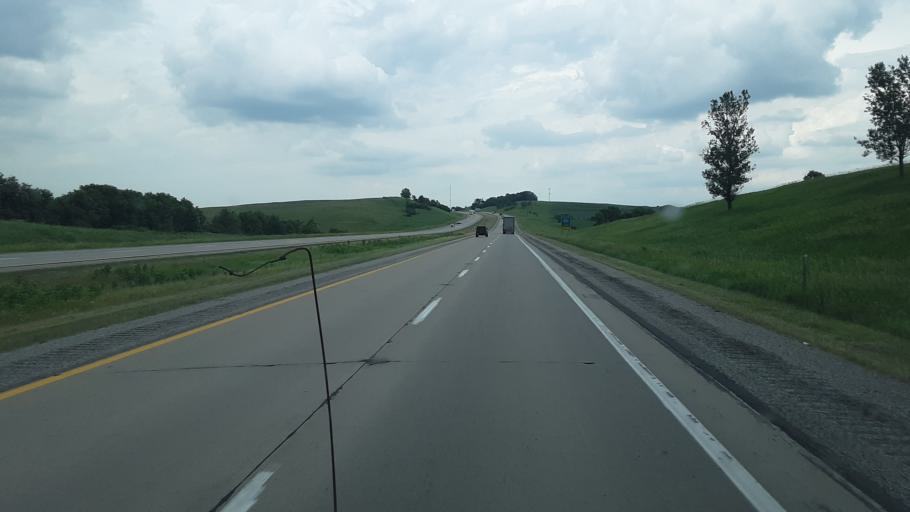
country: US
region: Iowa
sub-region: Pottawattamie County
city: Avoca
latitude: 41.4722
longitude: -95.5918
